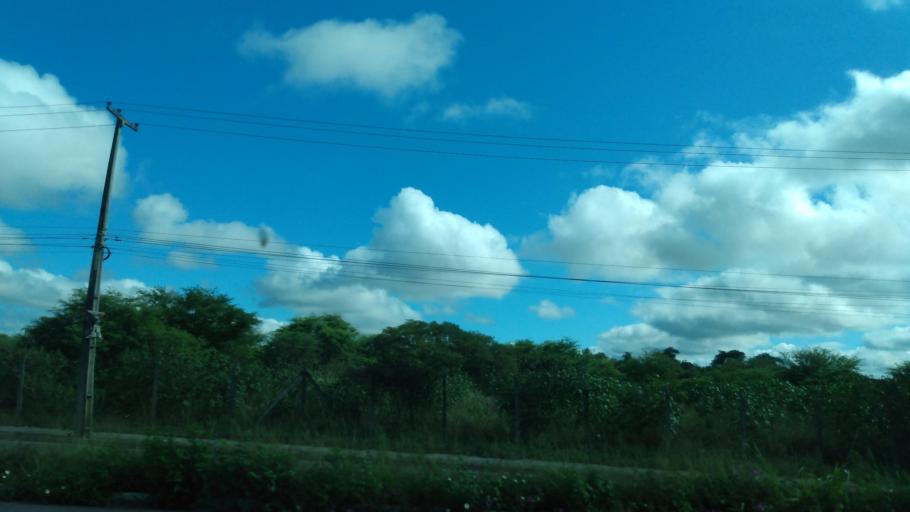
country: BR
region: Pernambuco
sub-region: Caruaru
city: Caruaru
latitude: -8.3015
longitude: -36.0001
